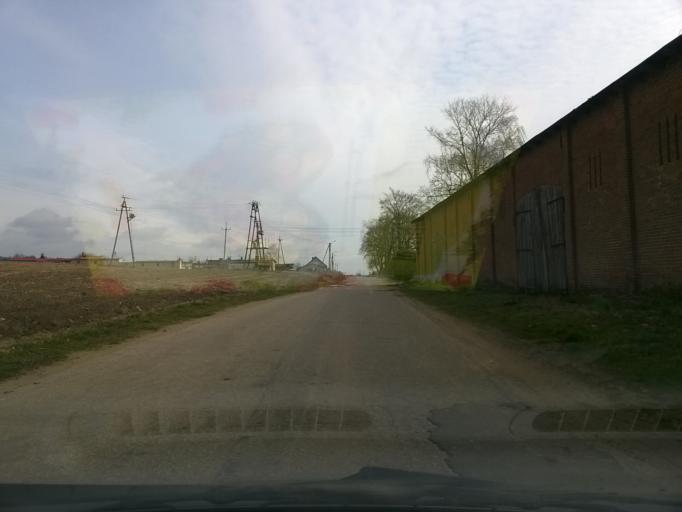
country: PL
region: Greater Poland Voivodeship
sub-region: Powiat wagrowiecki
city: Golancz
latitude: 52.9823
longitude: 17.3398
